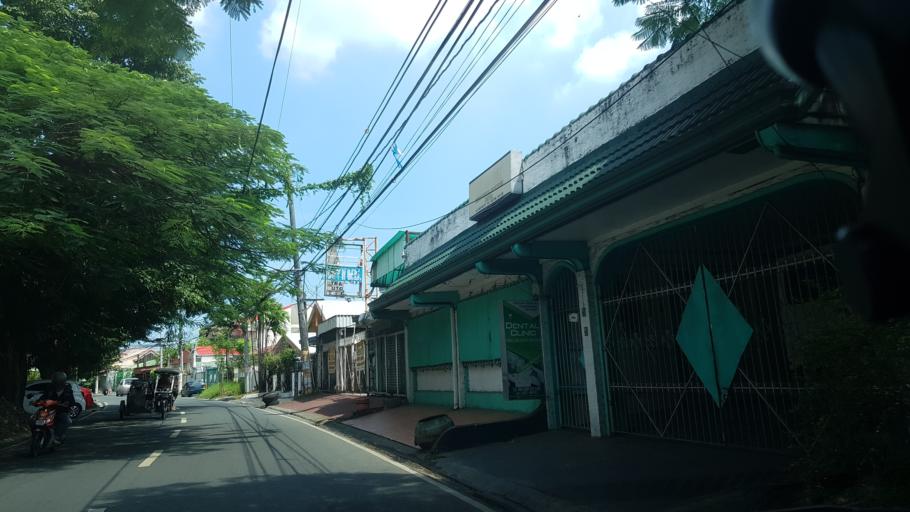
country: PH
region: Calabarzon
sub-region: Province of Rizal
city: Las Pinas
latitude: 14.4327
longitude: 120.9943
